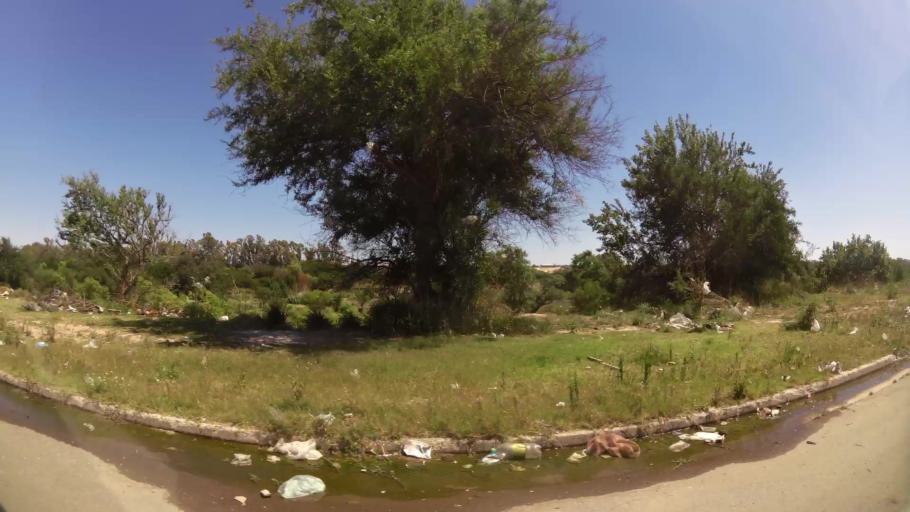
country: AR
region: Cordoba
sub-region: Departamento de Capital
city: Cordoba
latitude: -31.4076
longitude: -64.1407
